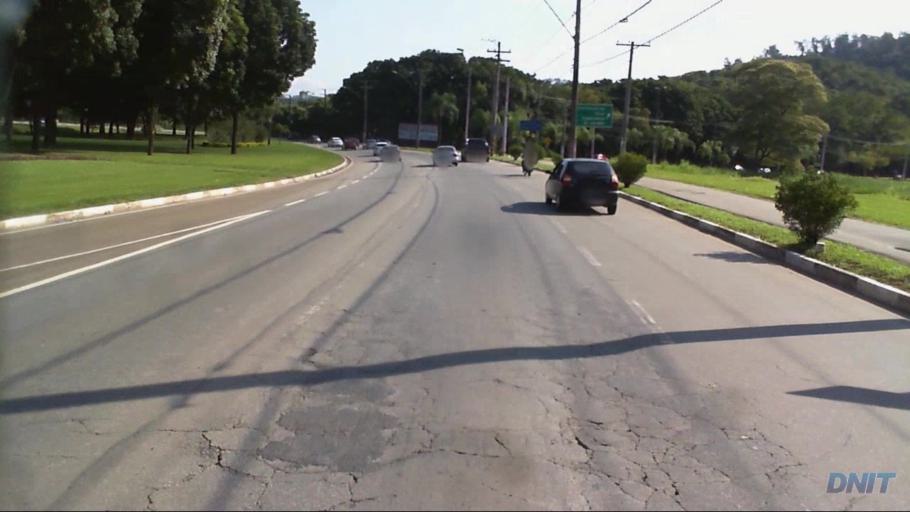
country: BR
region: Minas Gerais
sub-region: Ipatinga
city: Ipatinga
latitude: -19.4839
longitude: -42.5541
